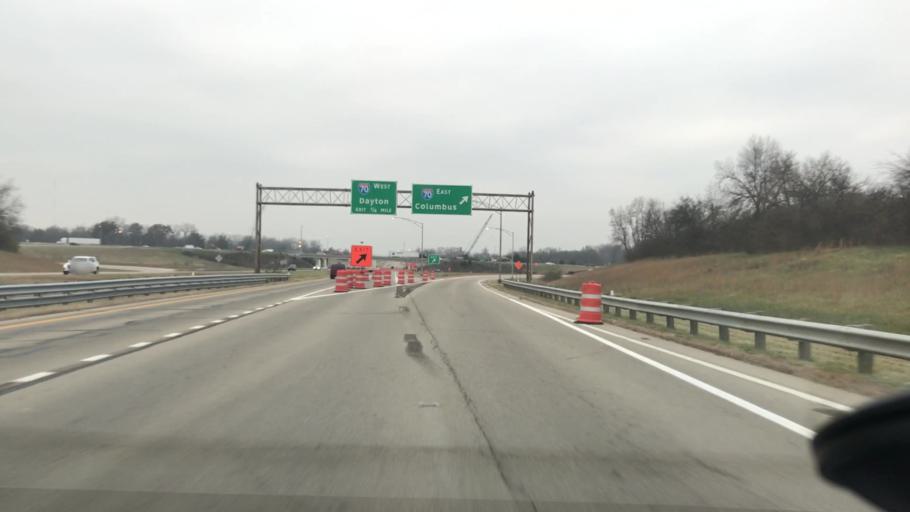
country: US
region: Ohio
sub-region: Clark County
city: Springfield
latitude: 39.8910
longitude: -83.8538
